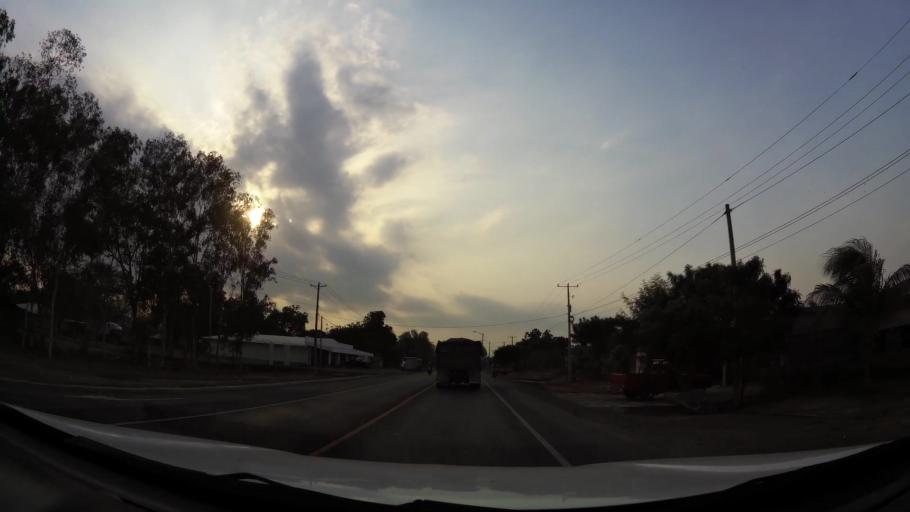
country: NI
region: Managua
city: Ciudad Sandino
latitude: 12.1834
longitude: -86.3591
